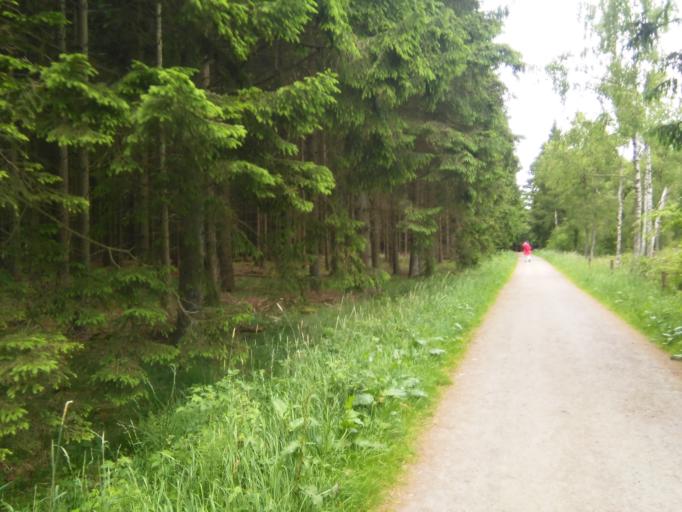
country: DK
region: Capital Region
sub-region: Bornholm Kommune
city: Akirkeby
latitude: 55.1123
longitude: 14.9418
